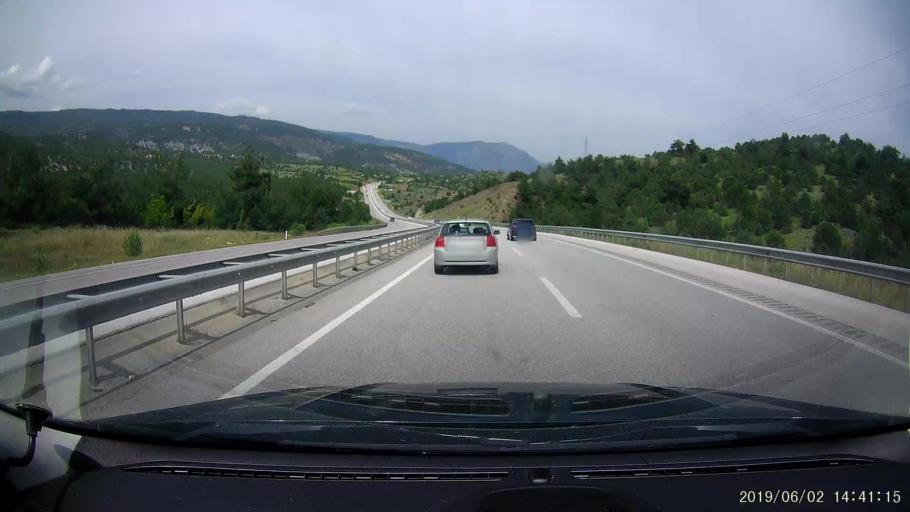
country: TR
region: Corum
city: Hacihamza
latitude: 41.0840
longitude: 34.3365
